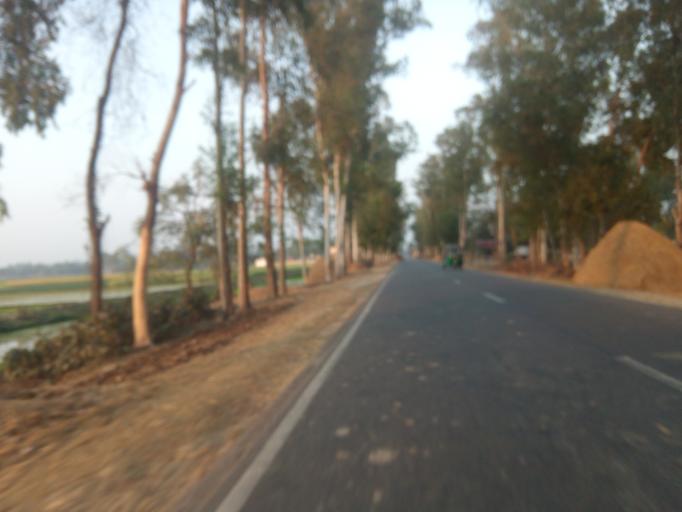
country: BD
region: Rajshahi
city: Bogra
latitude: 24.6349
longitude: 89.2483
